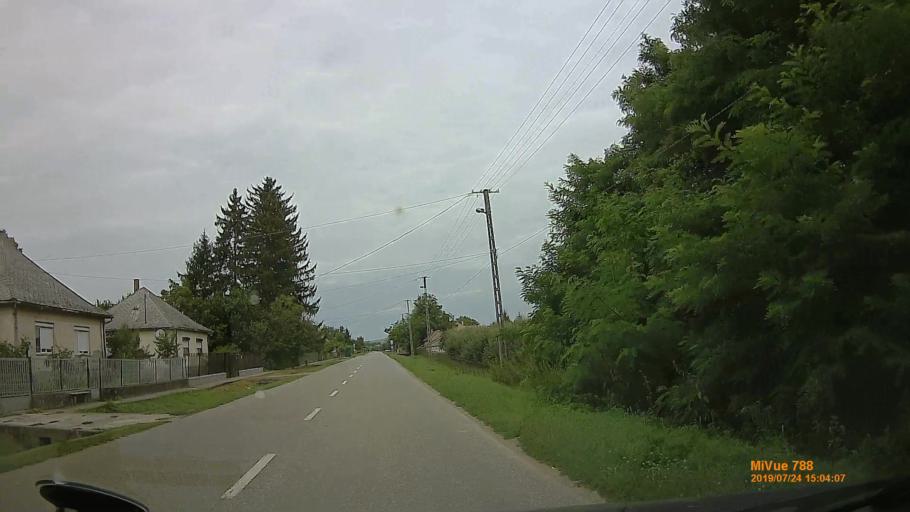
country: UA
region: Zakarpattia
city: Batiovo
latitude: 48.2247
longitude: 22.4188
